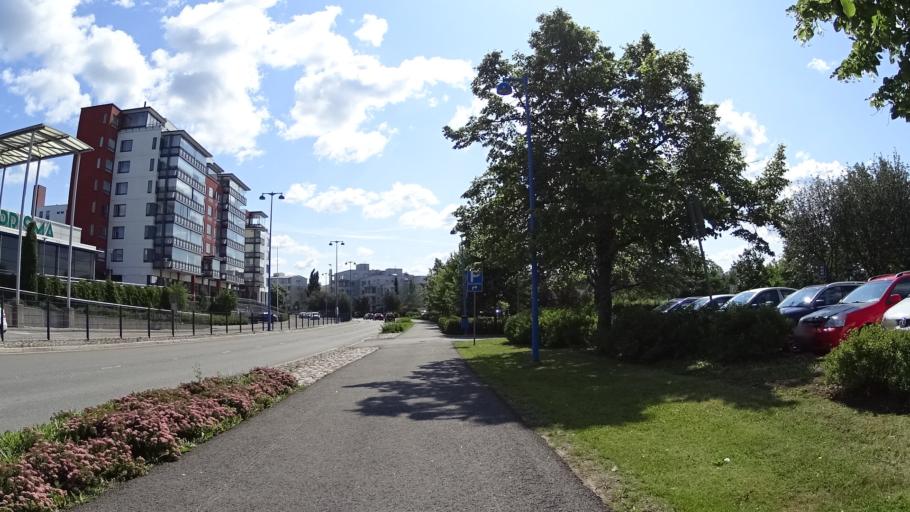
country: FI
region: Uusimaa
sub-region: Helsinki
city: Jaervenpaeae
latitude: 60.4699
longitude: 25.0830
